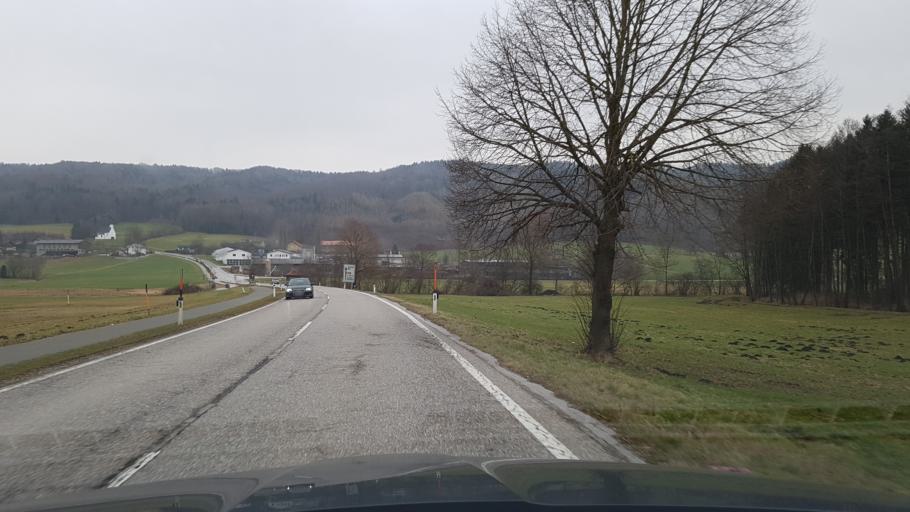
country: AT
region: Salzburg
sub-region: Politischer Bezirk Salzburg-Umgebung
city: Dorfbeuern
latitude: 48.0047
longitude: 13.0307
